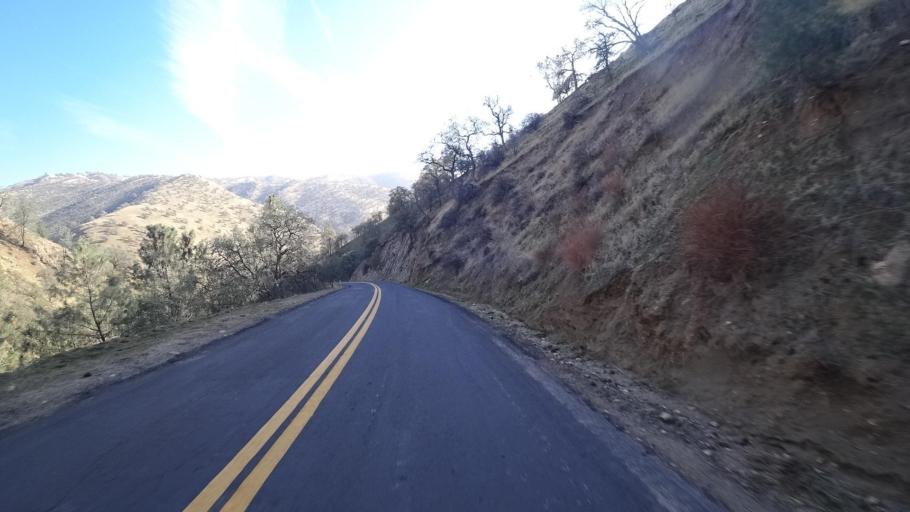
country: US
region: California
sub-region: Kern County
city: Bear Valley Springs
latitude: 35.3098
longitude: -118.5866
